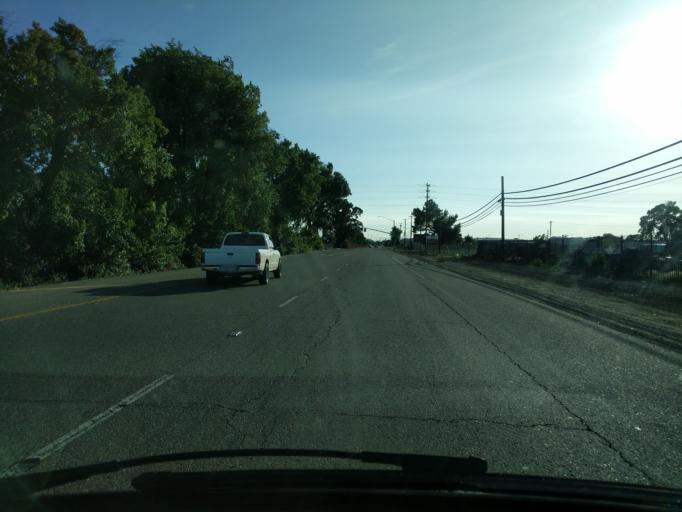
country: US
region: California
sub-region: San Joaquin County
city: Kennedy
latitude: 37.9445
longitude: -121.2578
